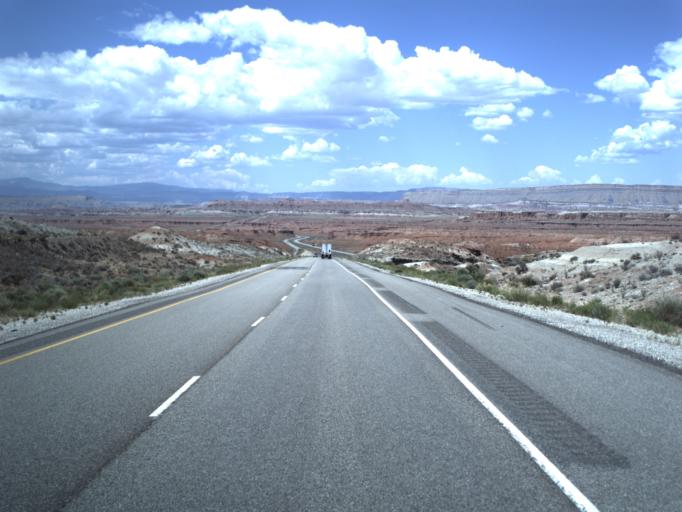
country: US
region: Utah
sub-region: Emery County
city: Ferron
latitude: 38.8479
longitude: -111.0147
